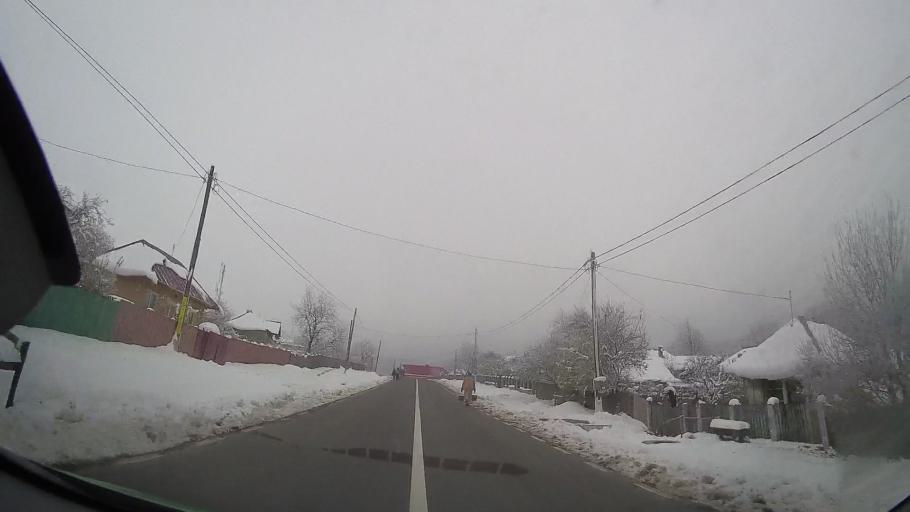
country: RO
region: Neamt
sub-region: Comuna Poenari
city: Poienari
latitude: 46.8800
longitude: 27.1321
